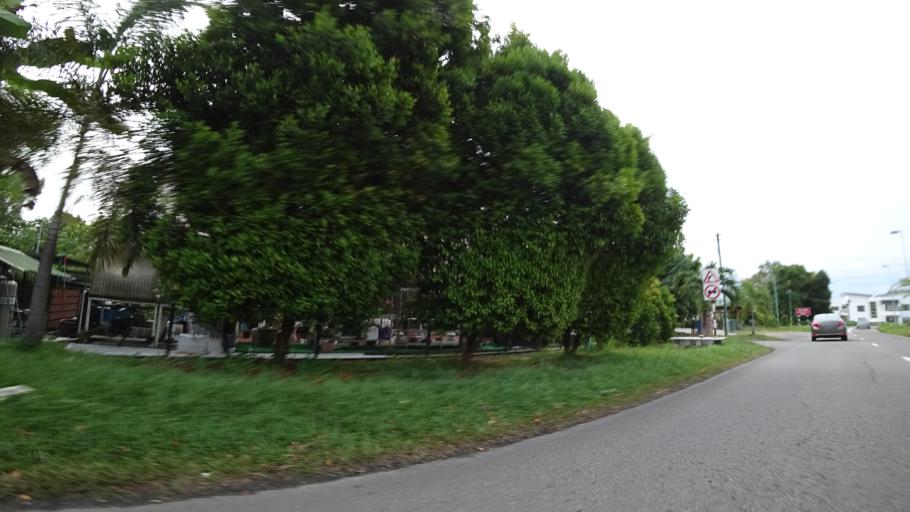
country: BN
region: Brunei and Muara
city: Bandar Seri Begawan
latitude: 4.9323
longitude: 114.9491
